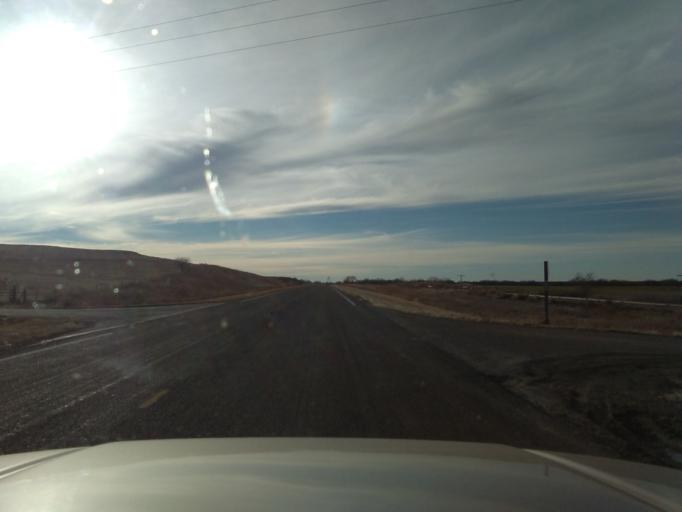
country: US
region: Kansas
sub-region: Norton County
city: Norton
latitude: 39.7477
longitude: -100.1521
